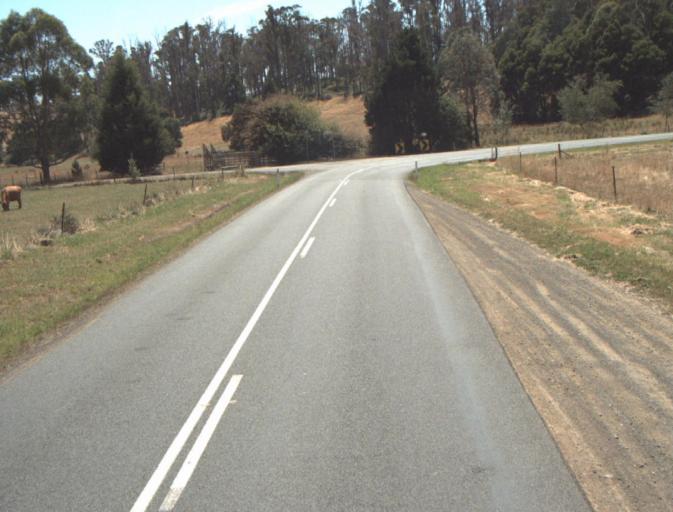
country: AU
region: Tasmania
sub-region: Launceston
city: Mayfield
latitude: -41.2597
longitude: 147.1359
